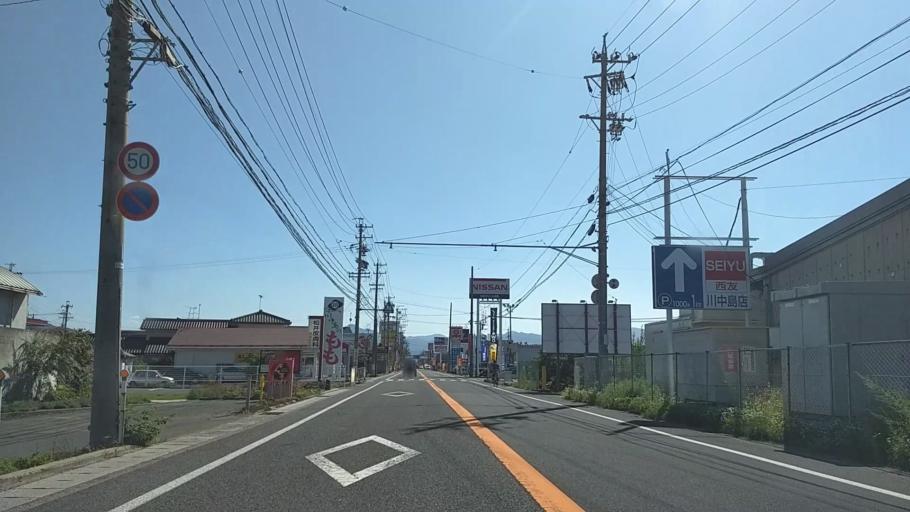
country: JP
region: Nagano
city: Nagano-shi
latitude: 36.6021
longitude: 138.1604
